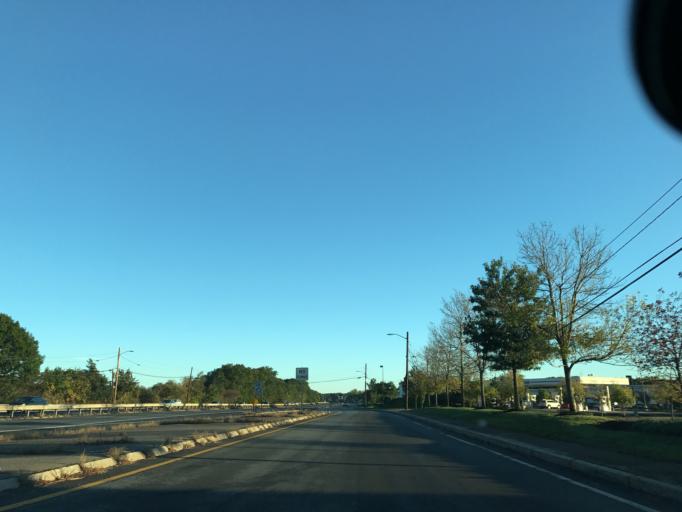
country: US
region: Massachusetts
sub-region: Norfolk County
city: Dedham
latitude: 42.2566
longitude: -71.1703
